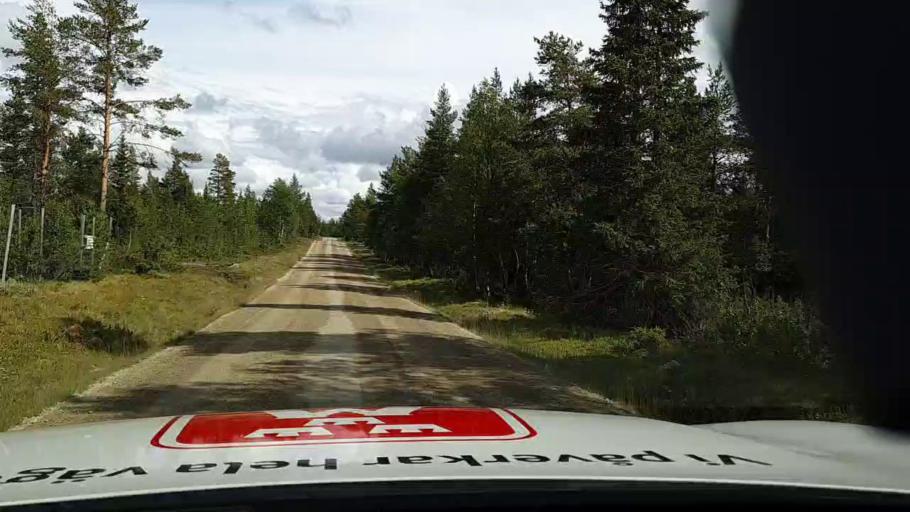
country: SE
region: Jaemtland
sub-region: Are Kommun
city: Jarpen
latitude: 62.5483
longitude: 13.4574
